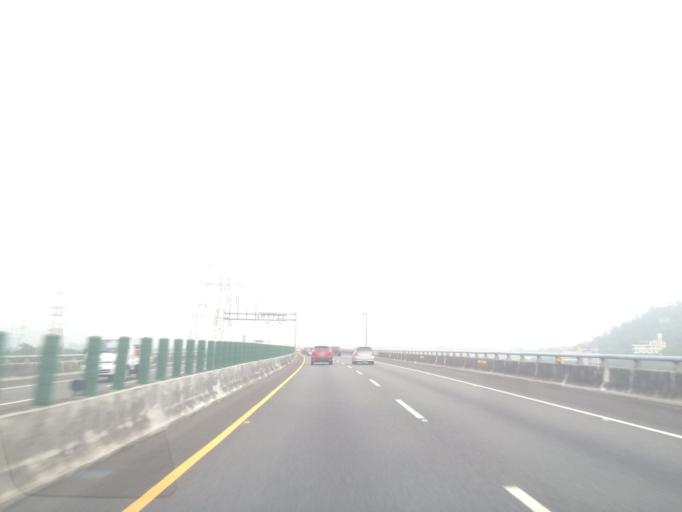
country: TW
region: Taiwan
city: Zhongxing New Village
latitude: 24.0078
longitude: 120.7070
